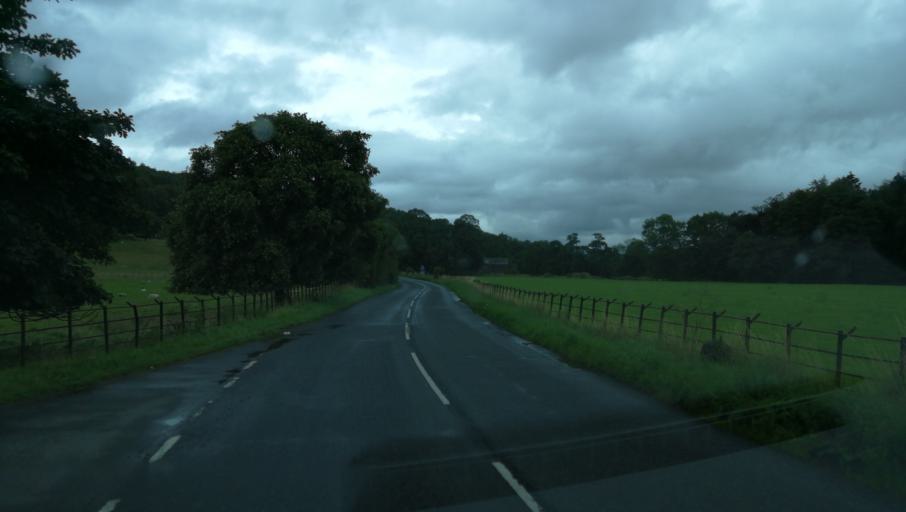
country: GB
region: England
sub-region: Cumbria
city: Penrith
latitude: 54.6346
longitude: -2.8079
